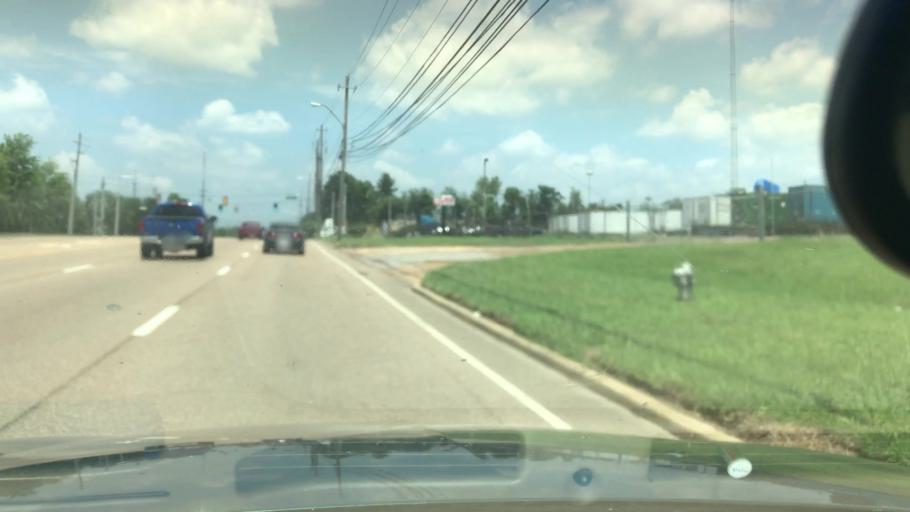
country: US
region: Mississippi
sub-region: De Soto County
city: Southaven
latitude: 35.0229
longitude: -89.9368
